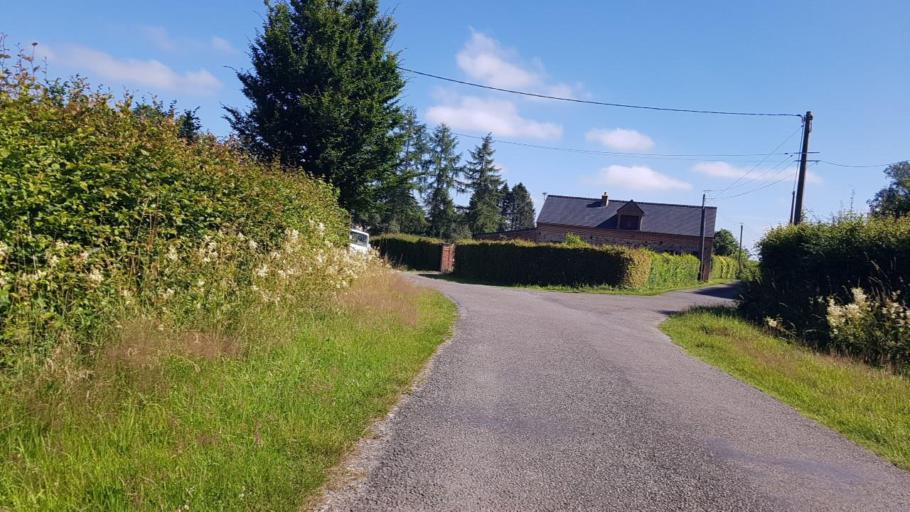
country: FR
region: Nord-Pas-de-Calais
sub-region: Departement du Nord
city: Anor
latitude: 49.9867
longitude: 4.1274
